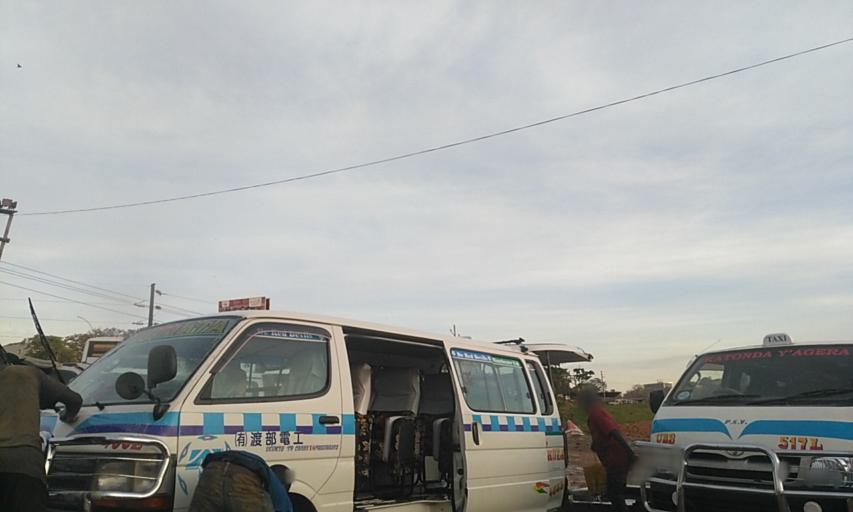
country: UG
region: Central Region
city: Kampala Central Division
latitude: 0.3392
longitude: 32.5728
